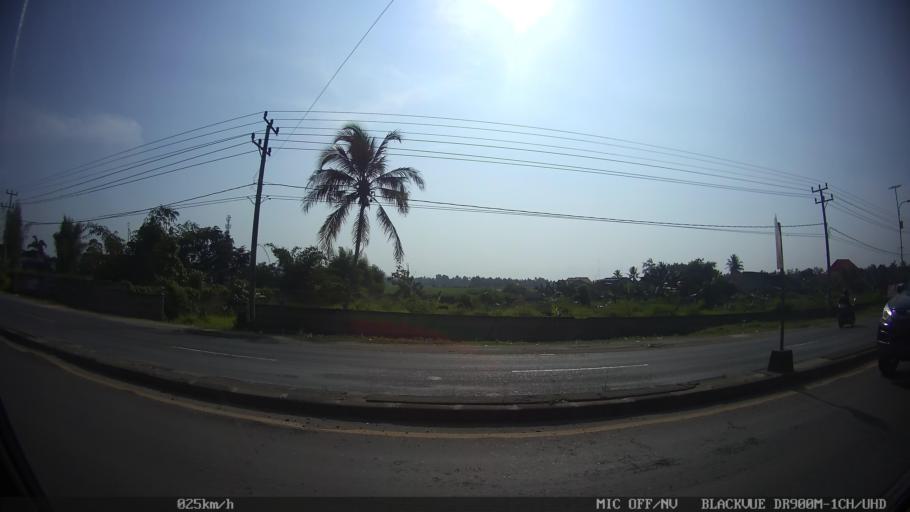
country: ID
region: Lampung
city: Natar
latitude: -5.3053
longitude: 105.1918
